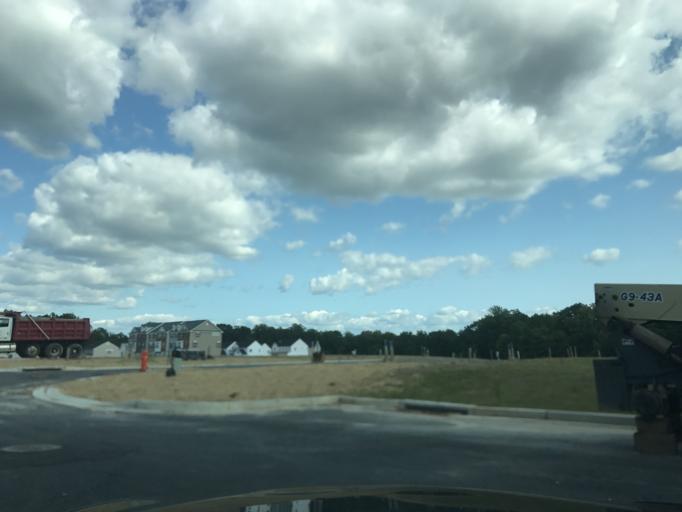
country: US
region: Maryland
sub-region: Baltimore County
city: Middle River
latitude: 39.3539
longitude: -76.4222
